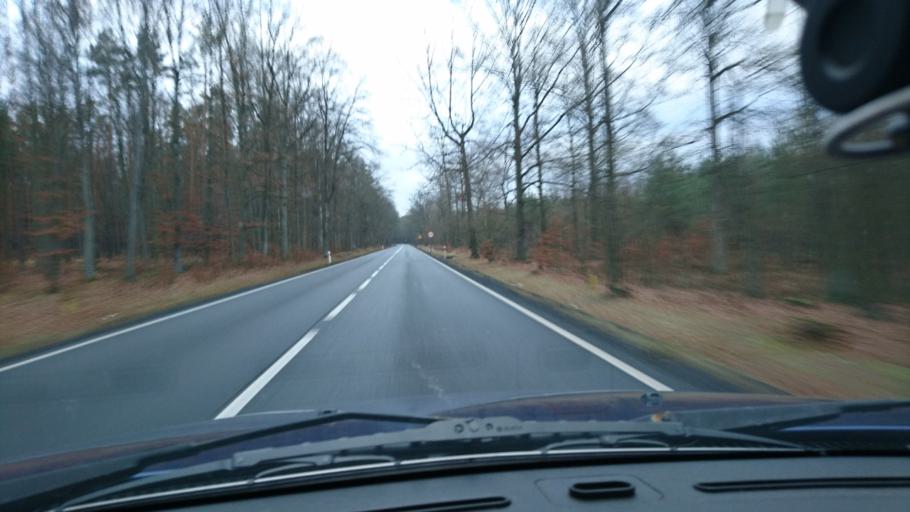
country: PL
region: Opole Voivodeship
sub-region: Powiat oleski
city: Olesno
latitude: 50.9333
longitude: 18.3322
